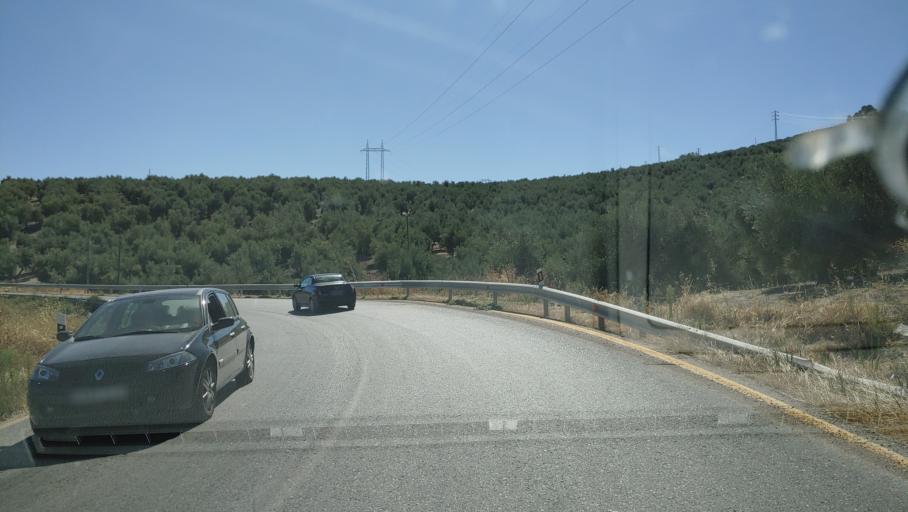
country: ES
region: Andalusia
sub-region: Provincia de Jaen
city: Iznatoraf
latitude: 38.1515
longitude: -3.0207
